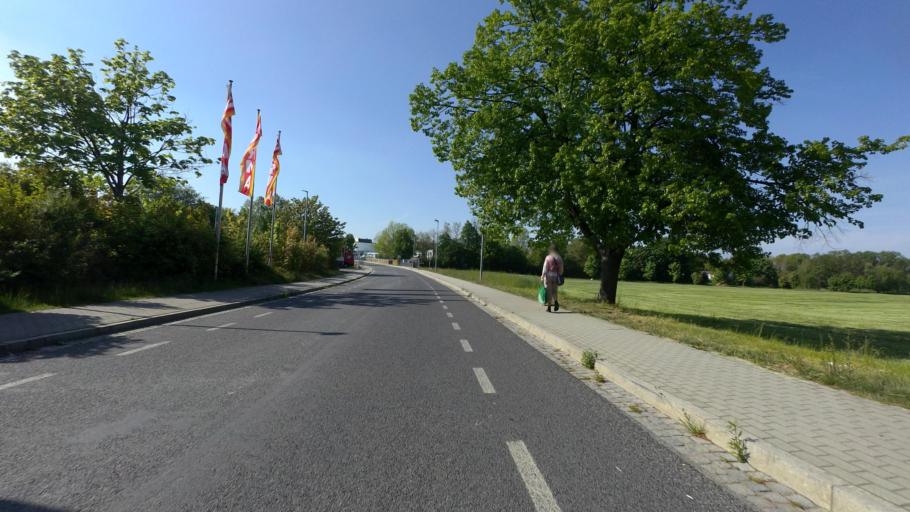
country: DE
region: Saxony
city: Kamenz
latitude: 51.2764
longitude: 14.1083
